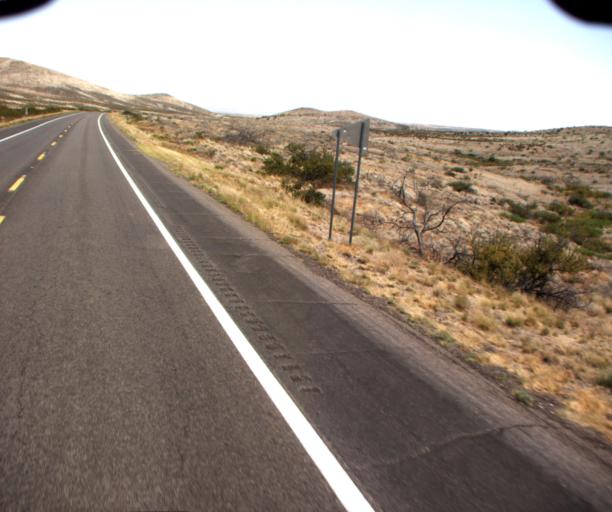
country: US
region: Arizona
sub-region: Greenlee County
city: Clifton
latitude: 32.7447
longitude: -109.2175
